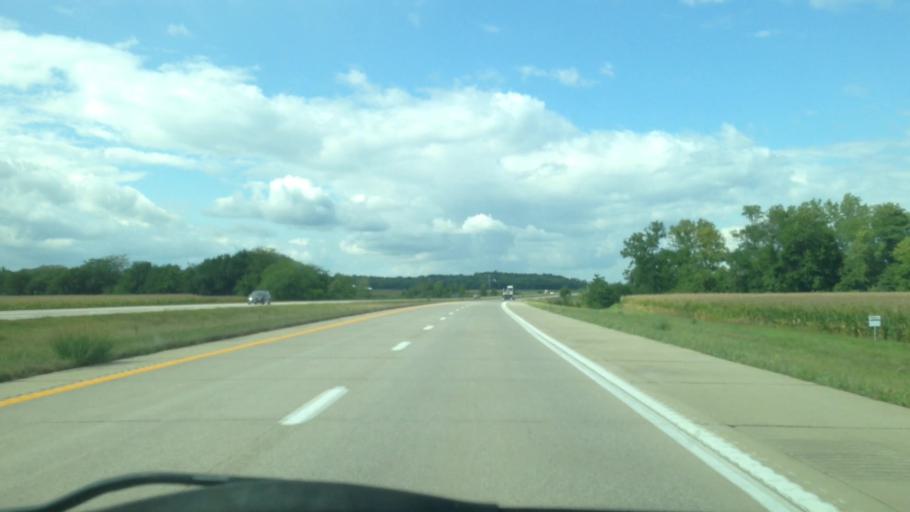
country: US
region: Missouri
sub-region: Clark County
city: Kahoka
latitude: 40.4164
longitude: -91.5724
